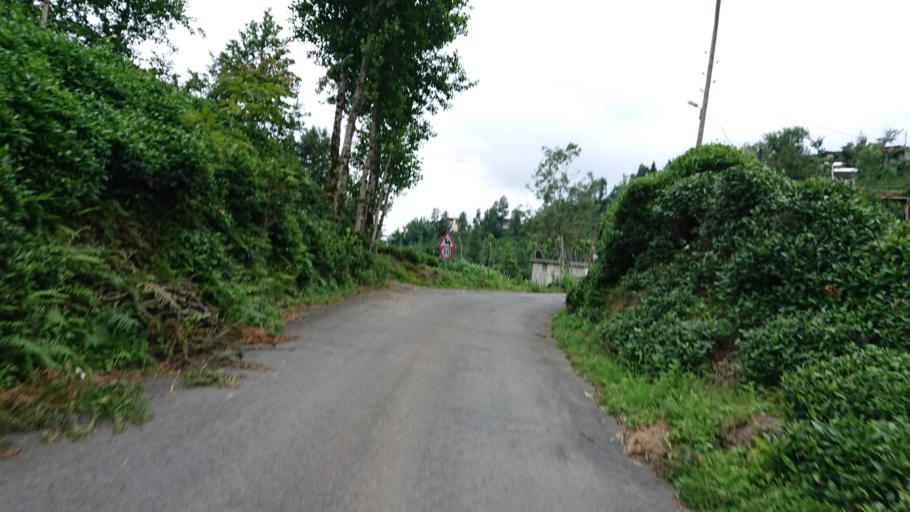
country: TR
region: Rize
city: Rize
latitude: 40.9740
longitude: 40.5165
